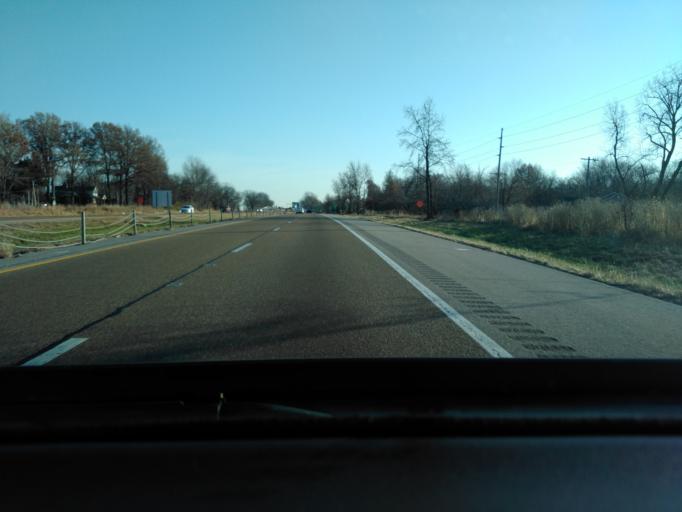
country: US
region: Illinois
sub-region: Madison County
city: Maryville
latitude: 38.7119
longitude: -89.9352
